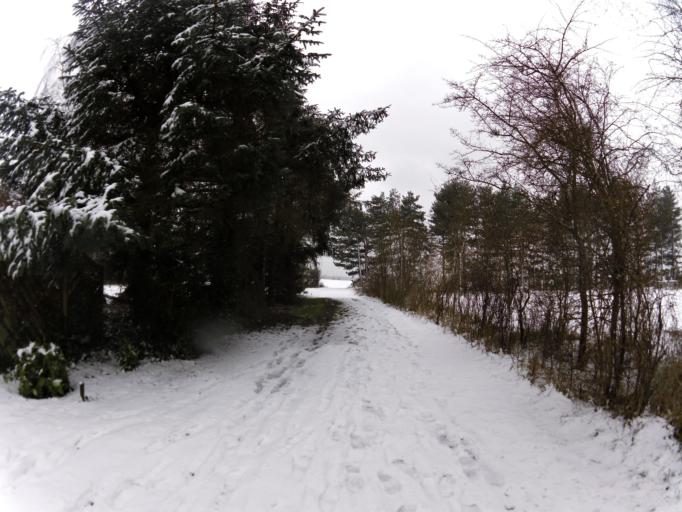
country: DK
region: Zealand
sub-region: Vordingborg Kommune
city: Neder Vindinge
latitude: 55.0514
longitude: 11.8329
